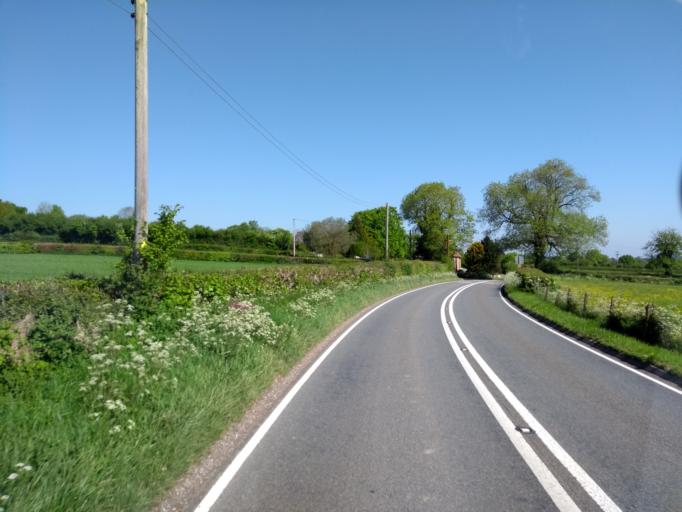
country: GB
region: England
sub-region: Somerset
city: Chard
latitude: 50.8412
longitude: -2.9600
